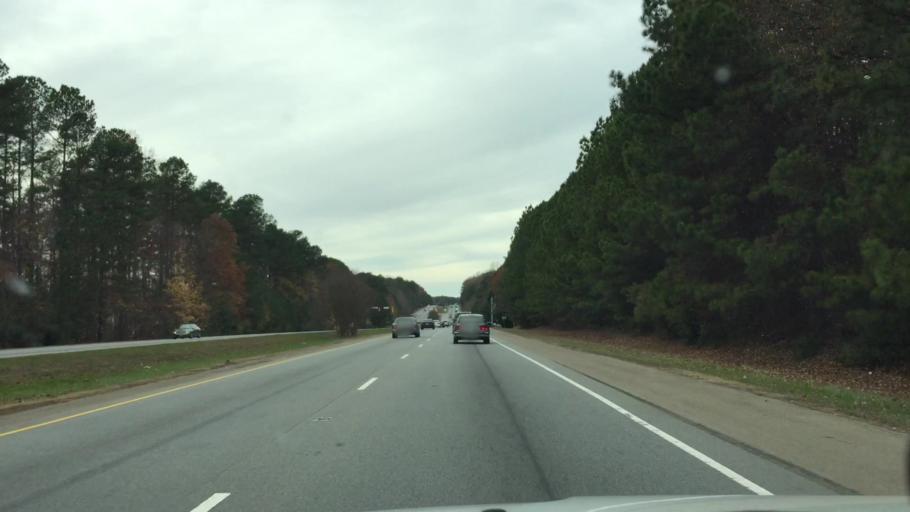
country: US
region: North Carolina
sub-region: Wake County
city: Apex
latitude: 35.7411
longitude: -78.8066
